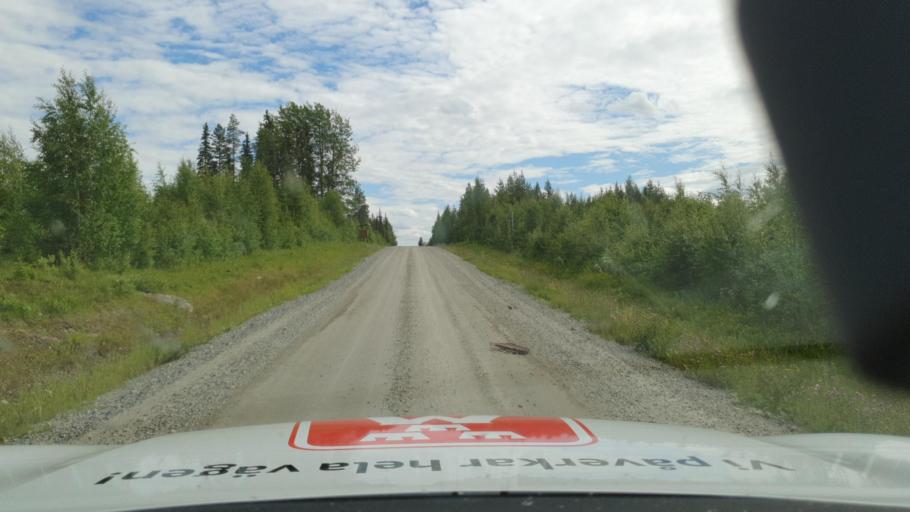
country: SE
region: Vaesterbotten
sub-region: Norsjo Kommun
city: Norsjoe
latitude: 64.8654
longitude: 19.4870
